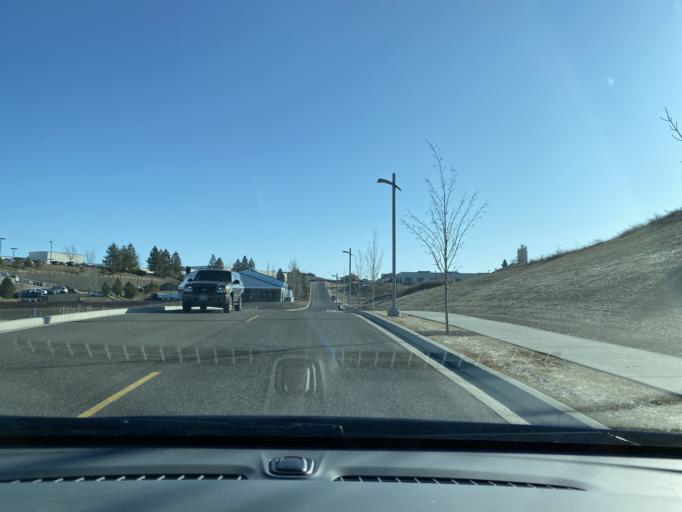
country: US
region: Washington
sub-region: Whitman County
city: Pullman
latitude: 46.7496
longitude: -117.1651
